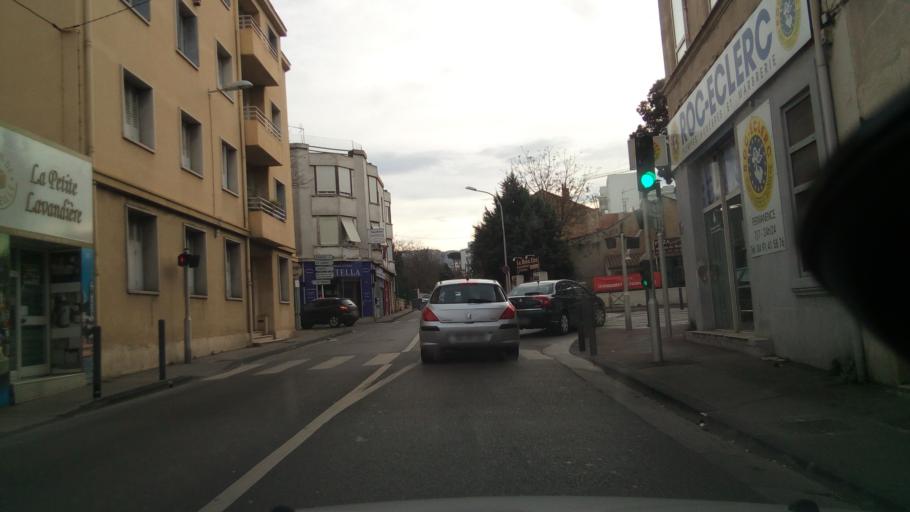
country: FR
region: Provence-Alpes-Cote d'Azur
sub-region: Departement des Bouches-du-Rhone
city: Marseille 09
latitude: 43.2650
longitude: 5.4091
